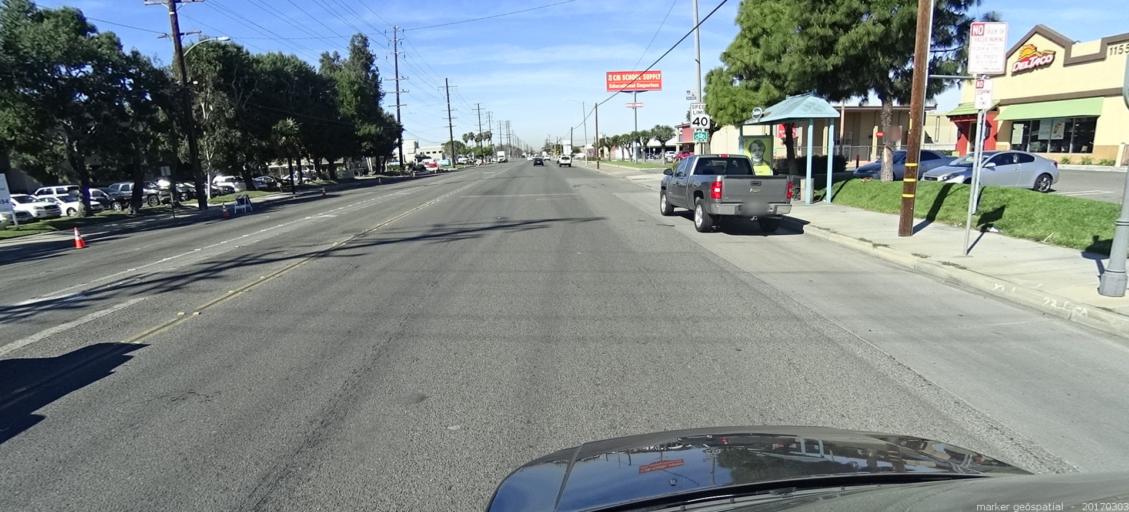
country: US
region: California
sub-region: Orange County
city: Fullerton
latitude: 33.8597
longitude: -117.9070
